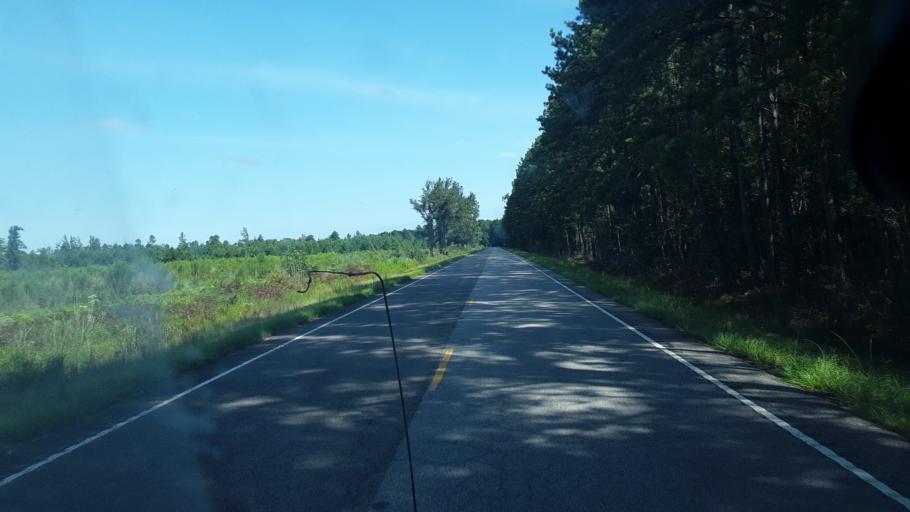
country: US
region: South Carolina
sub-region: Hampton County
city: Varnville
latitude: 32.8227
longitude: -81.0516
